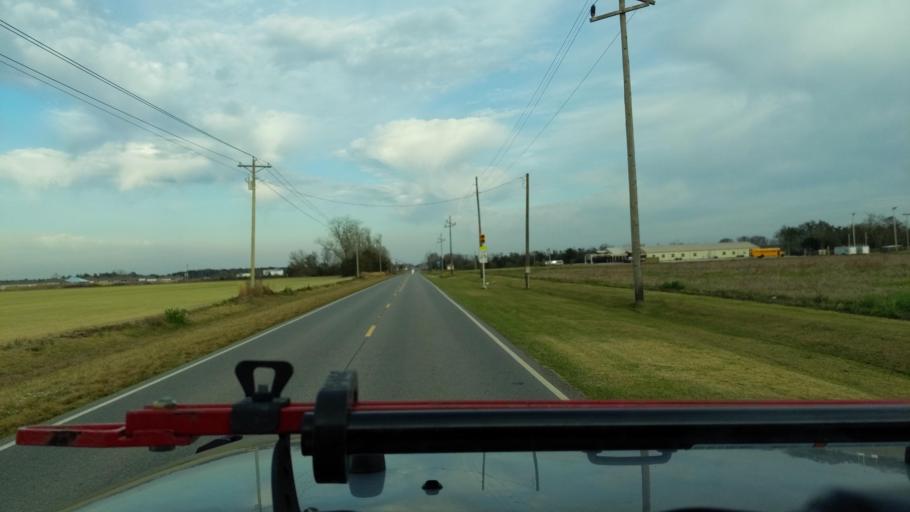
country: US
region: Alabama
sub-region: Baldwin County
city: Foley
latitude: 30.4580
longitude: -87.7040
